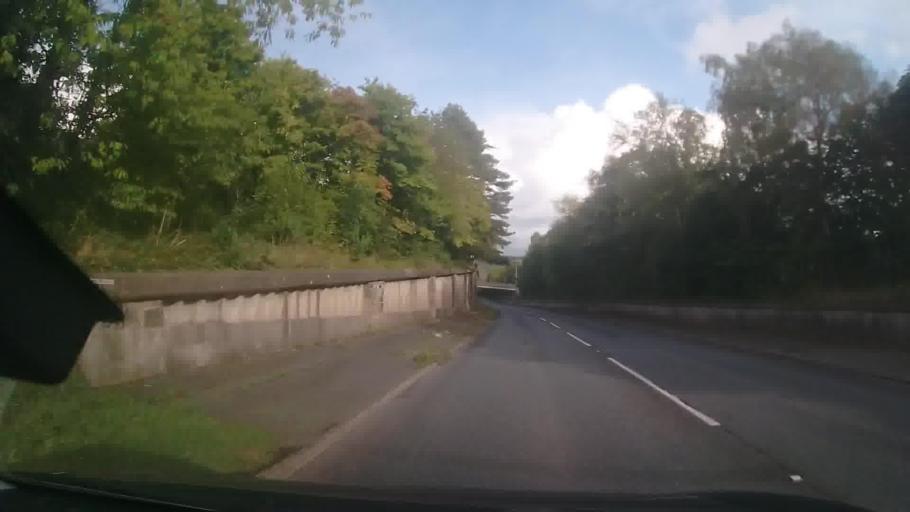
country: GB
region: Wales
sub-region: Gwynedd
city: Dolgellau
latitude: 52.7454
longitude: -3.8876
